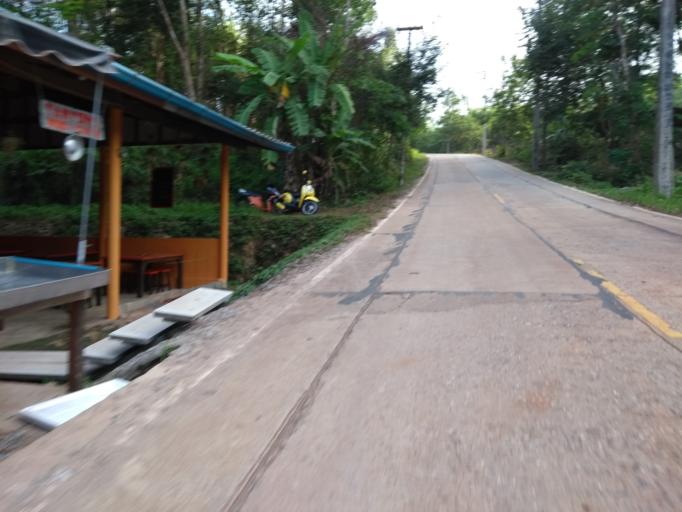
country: TH
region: Trat
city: Ko Kut
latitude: 11.6252
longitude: 102.5467
